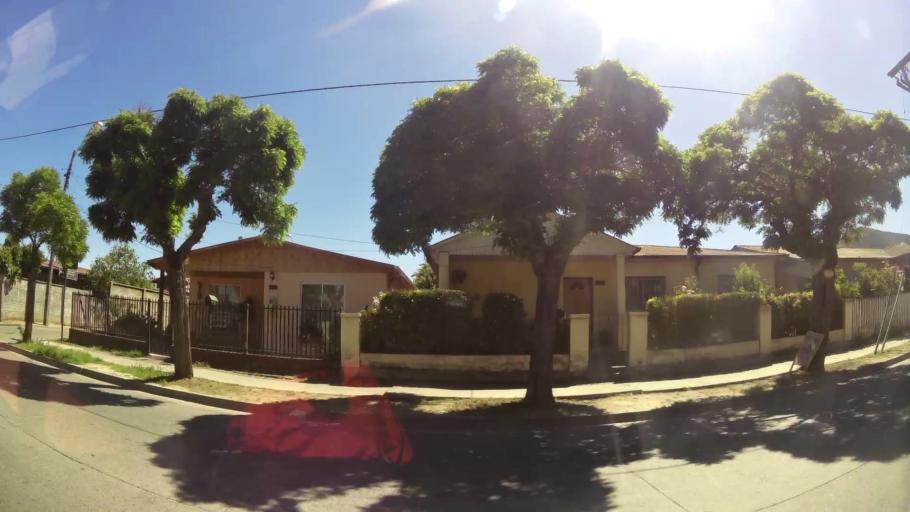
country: CL
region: Valparaiso
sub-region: Provincia de Marga Marga
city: Quilpue
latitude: -33.3171
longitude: -71.4012
